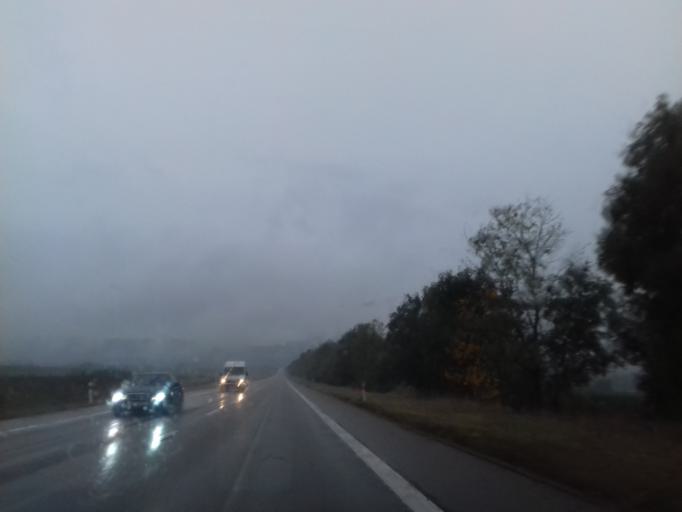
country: CZ
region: Pardubicky
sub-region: Okres Svitavy
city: Moravska Trebova
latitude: 49.7556
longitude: 16.6266
